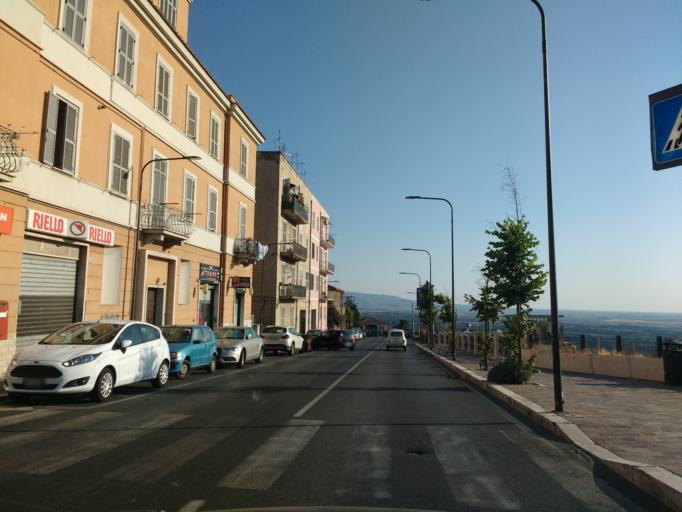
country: IT
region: Latium
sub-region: Citta metropolitana di Roma Capitale
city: Tivoli
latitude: 41.9572
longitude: 12.7929
